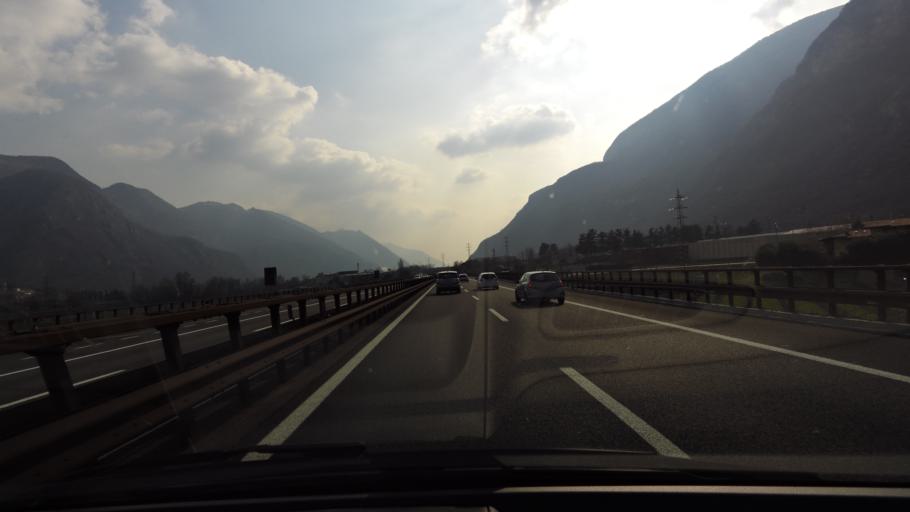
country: IT
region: Veneto
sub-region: Provincia di Verona
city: Rivalta
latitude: 45.6678
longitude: 10.8973
